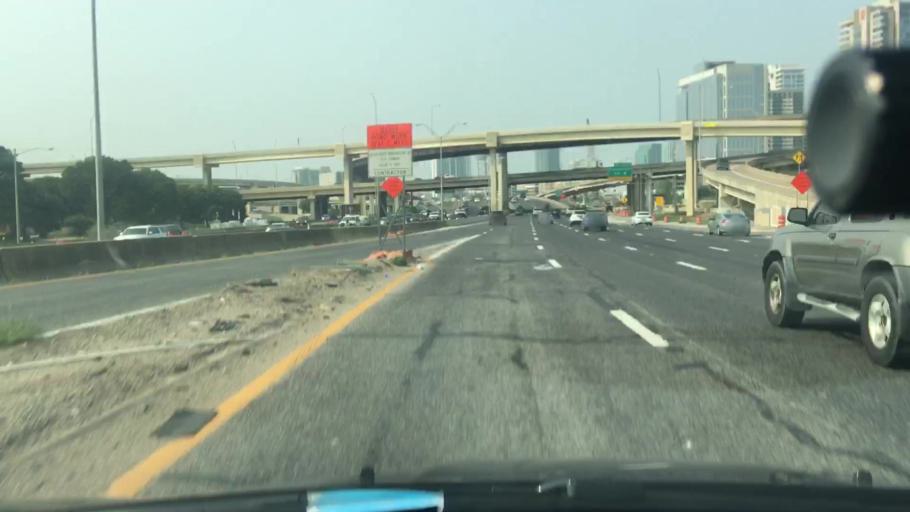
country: US
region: Texas
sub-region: Dallas County
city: Dallas
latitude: 32.7801
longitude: -96.8107
